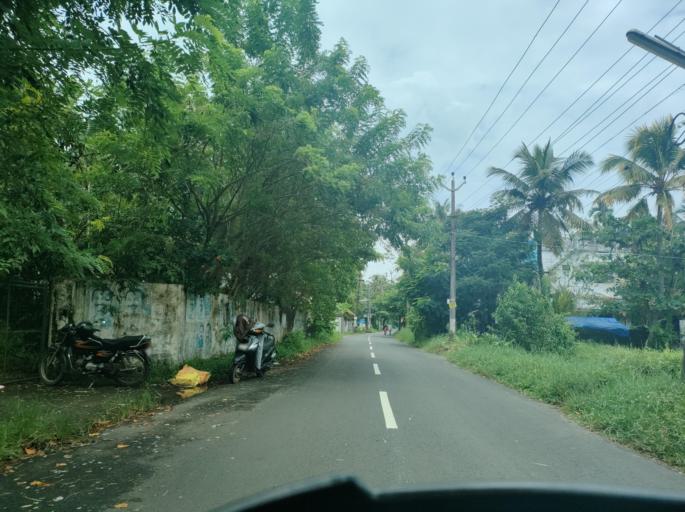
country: IN
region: Kerala
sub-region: Ernakulam
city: Elur
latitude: 10.0557
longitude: 76.2107
